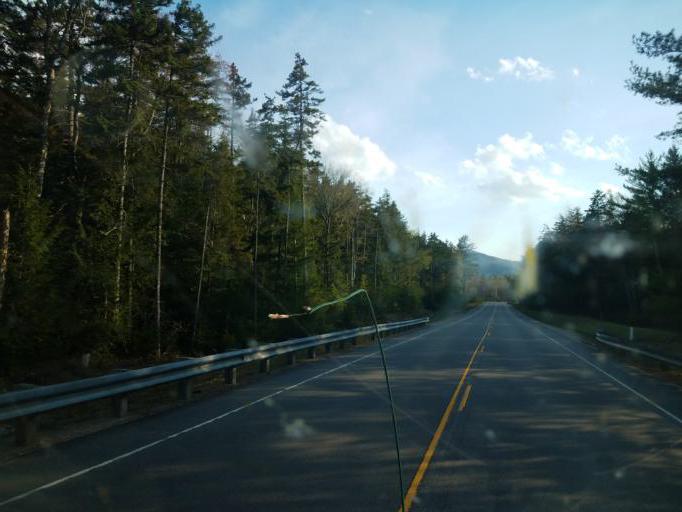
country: US
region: New Hampshire
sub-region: Carroll County
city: Tamworth
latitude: 43.9982
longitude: -71.2778
